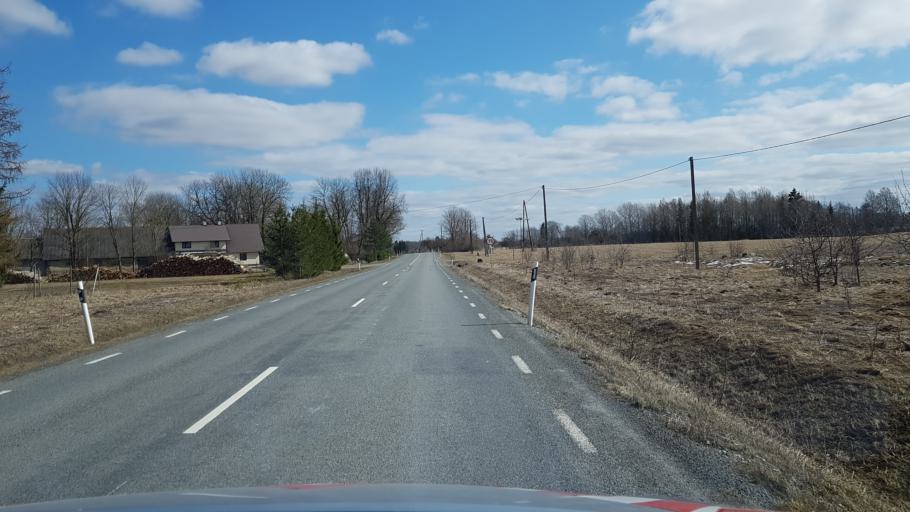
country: EE
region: Laeaene-Virumaa
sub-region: Tapa vald
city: Tapa
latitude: 59.2699
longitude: 25.9273
